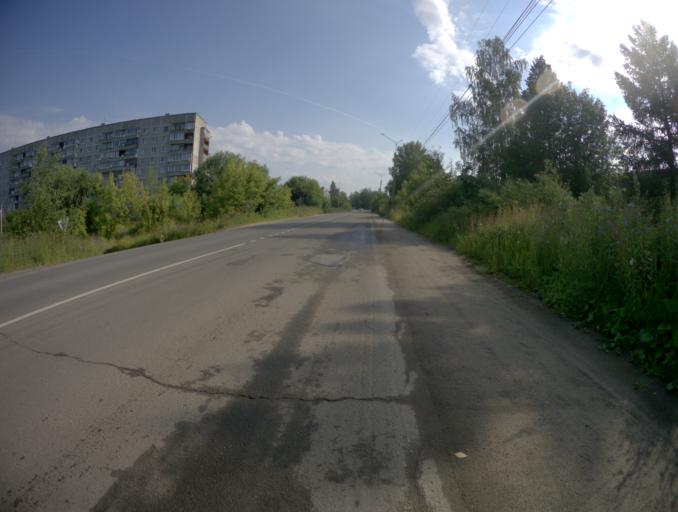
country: RU
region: Vladimir
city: Novovyazniki
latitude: 56.2281
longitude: 42.1942
